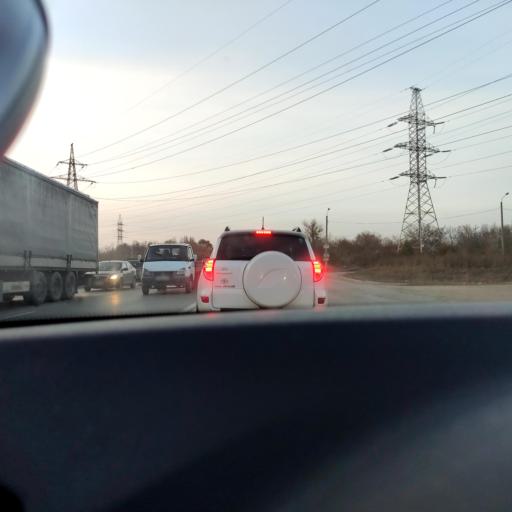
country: RU
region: Samara
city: Petra-Dubrava
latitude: 53.2590
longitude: 50.2927
